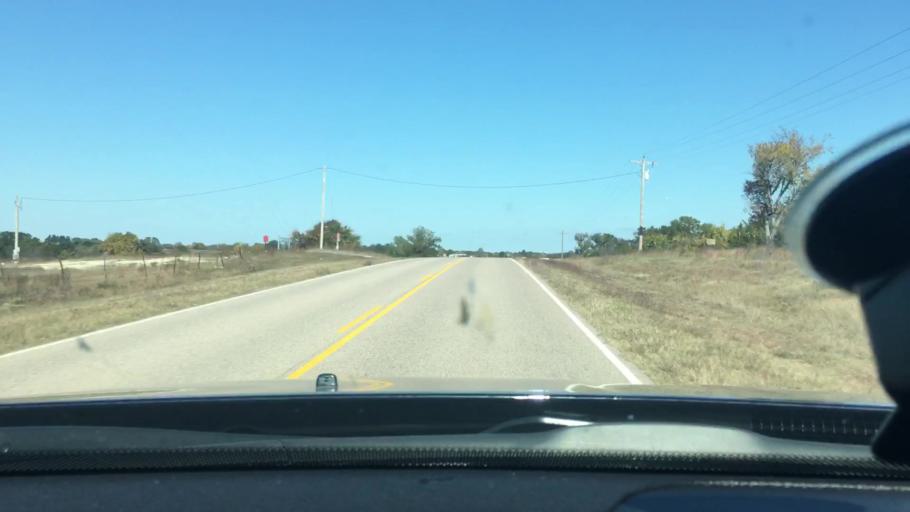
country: US
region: Oklahoma
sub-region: Johnston County
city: Tishomingo
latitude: 34.4312
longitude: -96.6360
